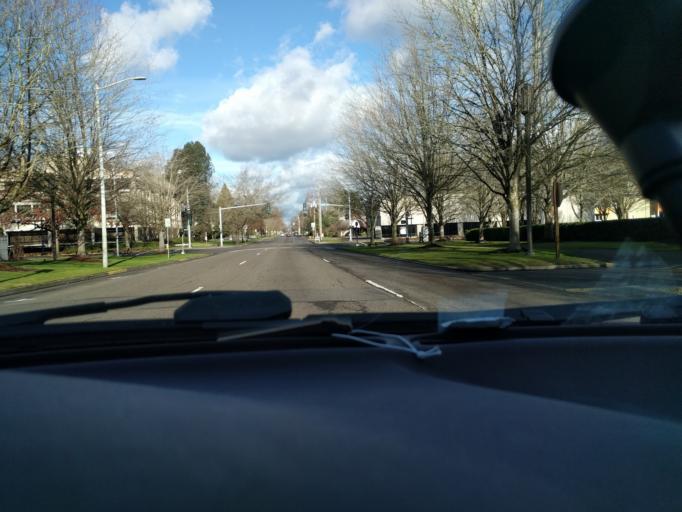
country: US
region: Oregon
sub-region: Marion County
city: Salem
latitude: 44.9425
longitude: -123.0266
